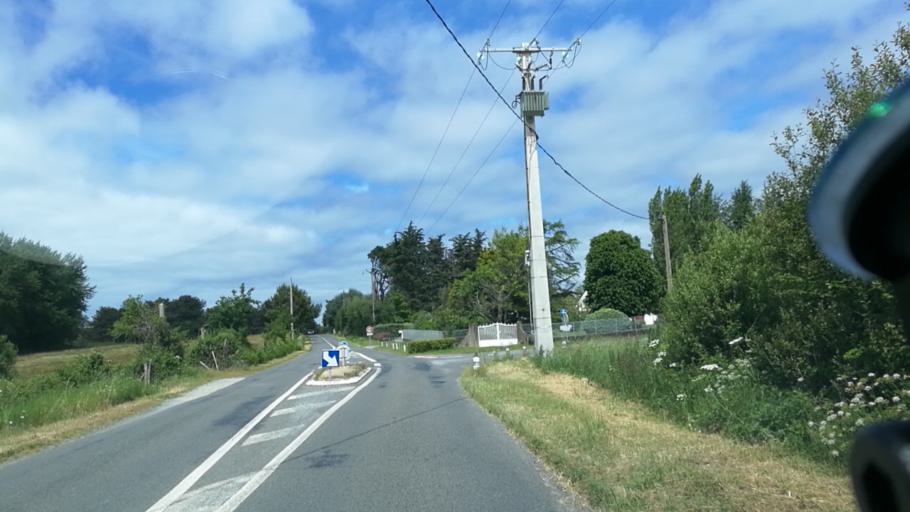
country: FR
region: Pays de la Loire
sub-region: Departement de la Loire-Atlantique
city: Mesquer
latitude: 47.4438
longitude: -2.4430
